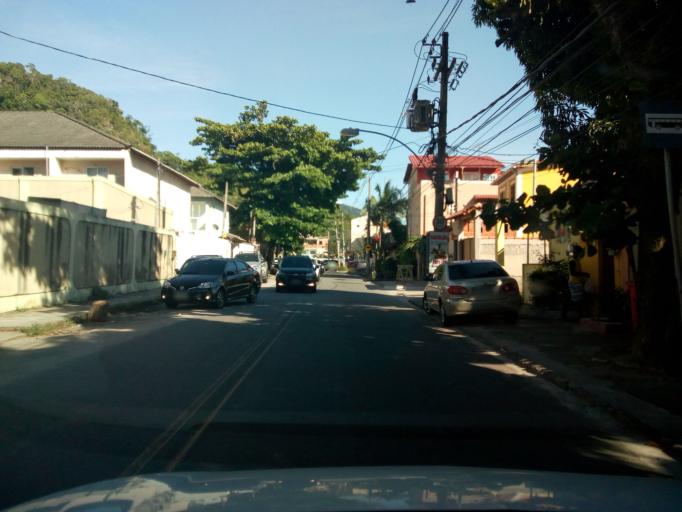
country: BR
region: Rio de Janeiro
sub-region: Nilopolis
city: Nilopolis
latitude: -23.0292
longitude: -43.4986
